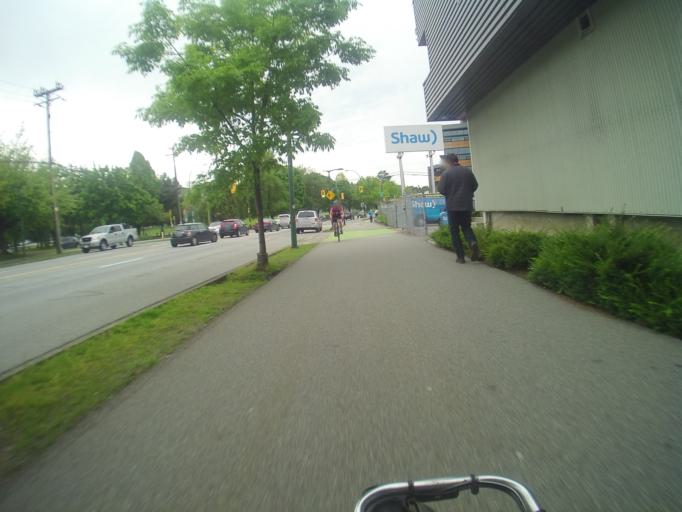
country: CA
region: British Columbia
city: Vancouver
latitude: 49.2653
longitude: -123.0805
